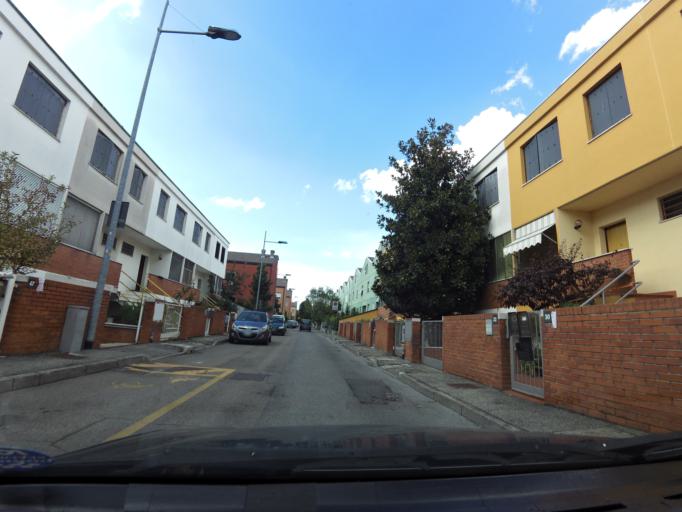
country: IT
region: Lombardy
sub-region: Citta metropolitana di Milano
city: Poasco-Sorigherio
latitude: 45.4030
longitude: 9.2313
